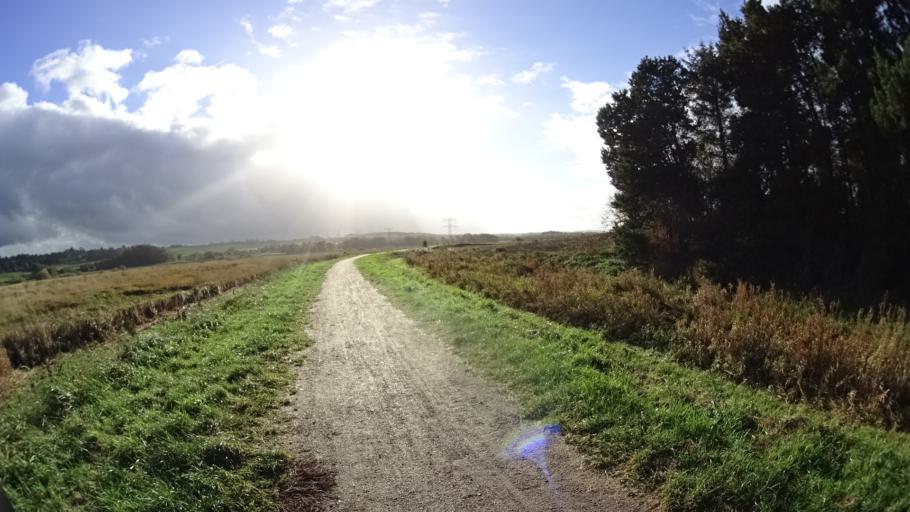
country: DK
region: Central Jutland
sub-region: Arhus Kommune
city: Kolt
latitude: 56.1367
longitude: 10.0503
